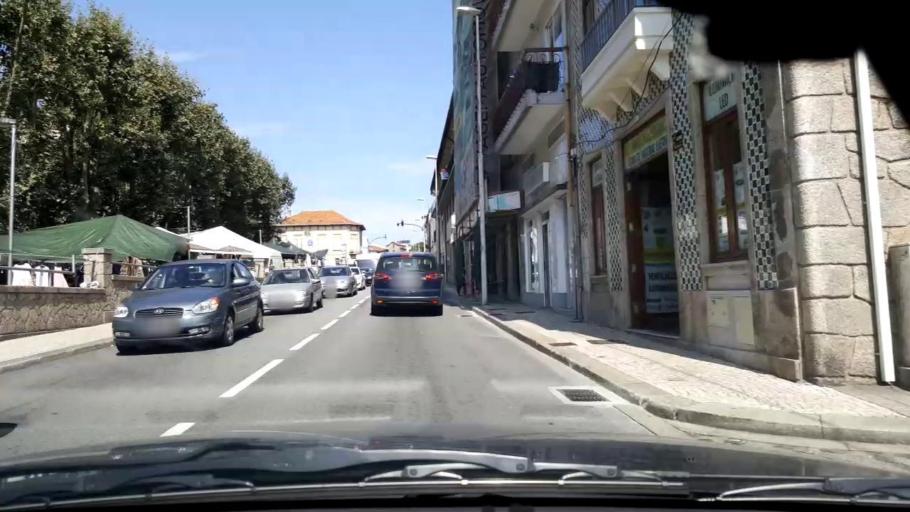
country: PT
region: Porto
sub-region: Vila do Conde
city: Vila do Conde
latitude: 41.3552
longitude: -8.7415
